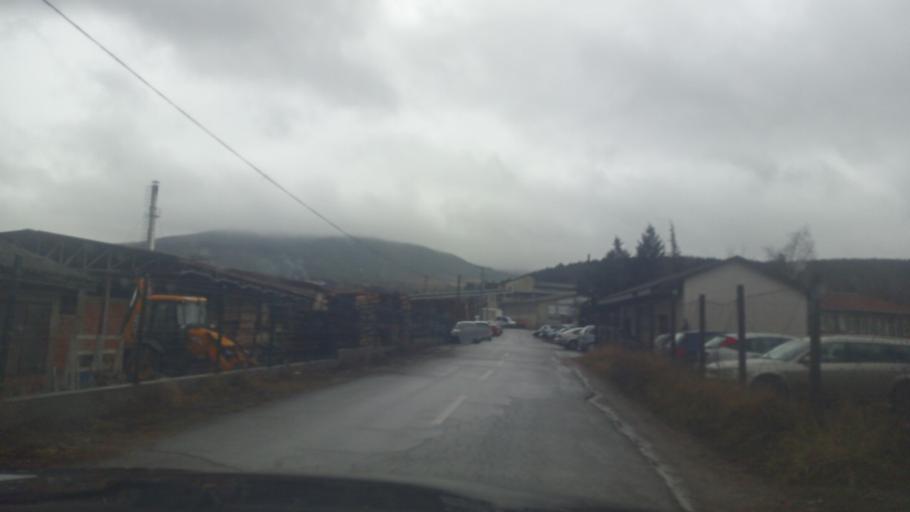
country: MK
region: Pehcevo
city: Pehcevo
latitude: 41.7601
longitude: 22.8818
